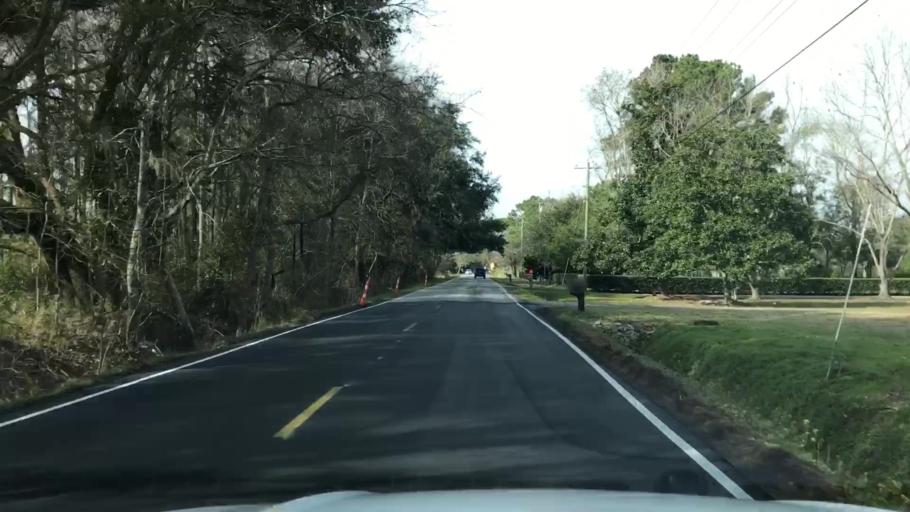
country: US
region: South Carolina
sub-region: Charleston County
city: Shell Point
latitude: 32.7665
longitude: -80.0679
